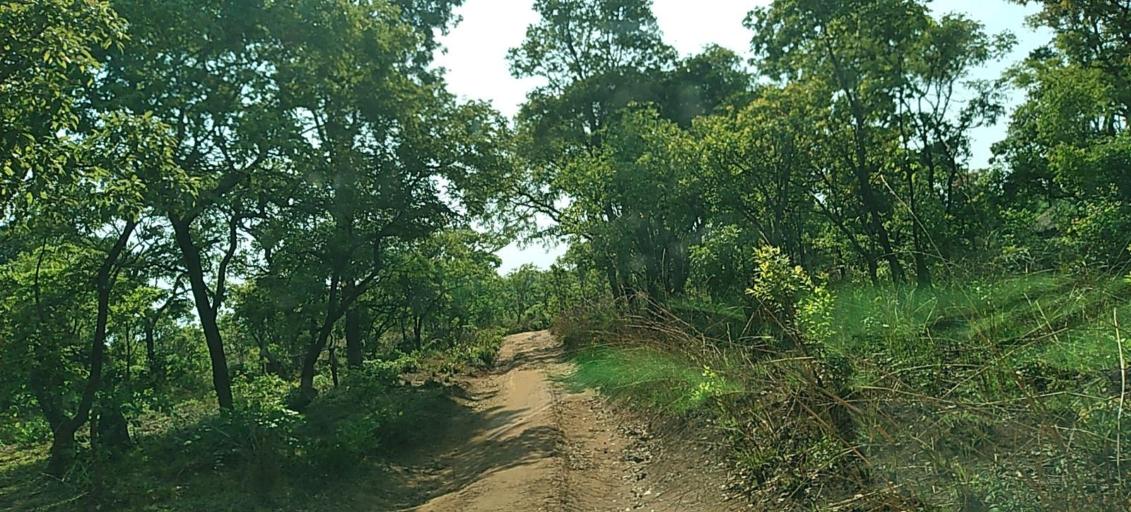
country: ZM
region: North-Western
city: Mwinilunga
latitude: -11.2981
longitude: 24.8634
